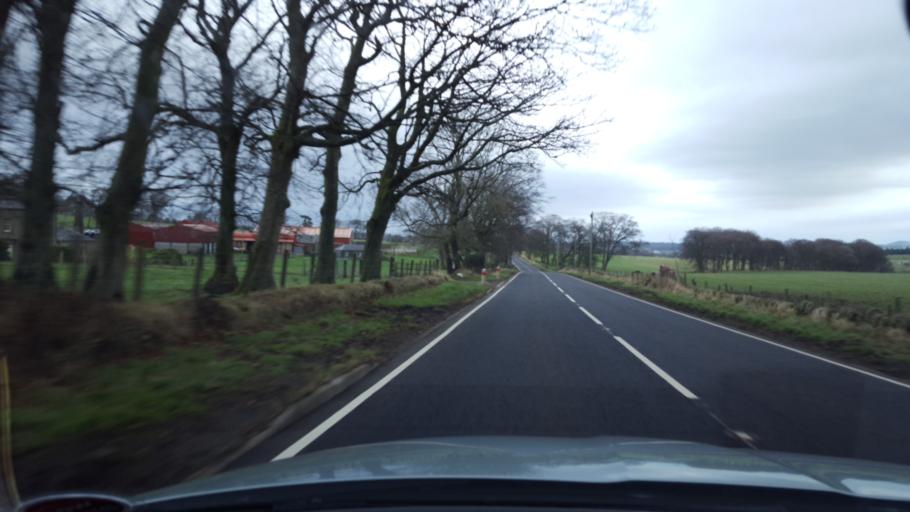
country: GB
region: Scotland
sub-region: West Lothian
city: Kirknewton
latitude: 55.8561
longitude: -3.4280
